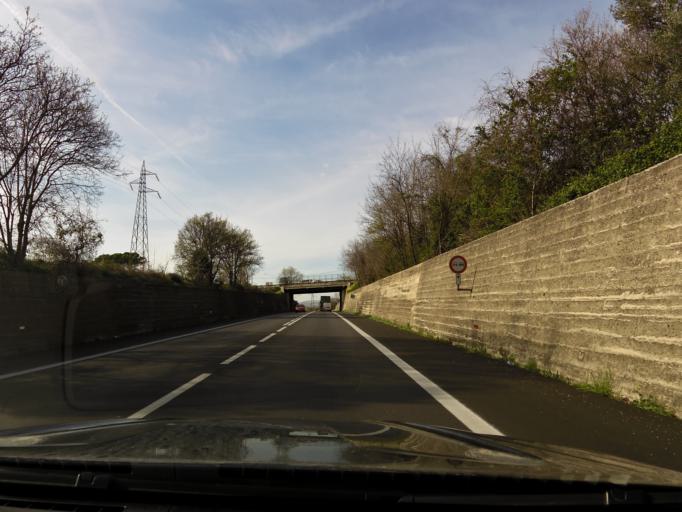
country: IT
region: The Marches
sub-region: Provincia di Ancona
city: Loreto Stazione
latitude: 43.4418
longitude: 13.6363
